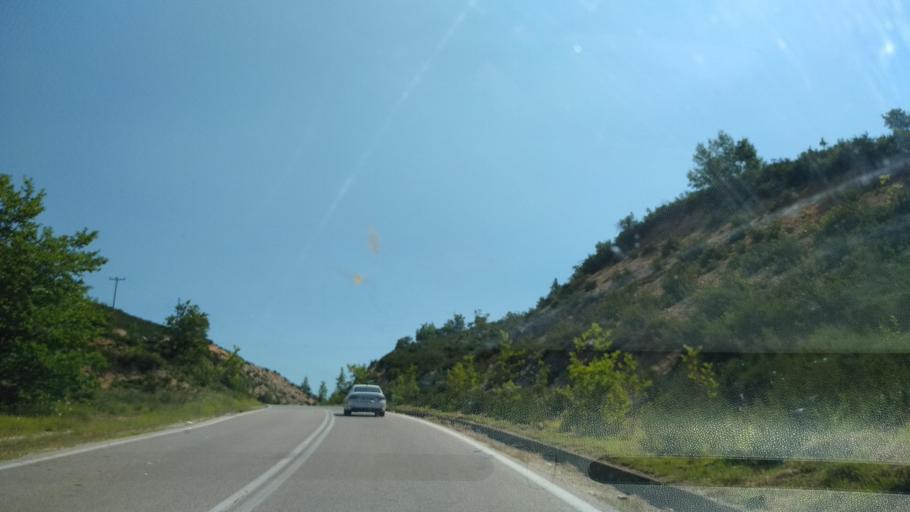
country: GR
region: Central Macedonia
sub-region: Nomos Chalkidikis
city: Arnaia
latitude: 40.4998
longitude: 23.5103
